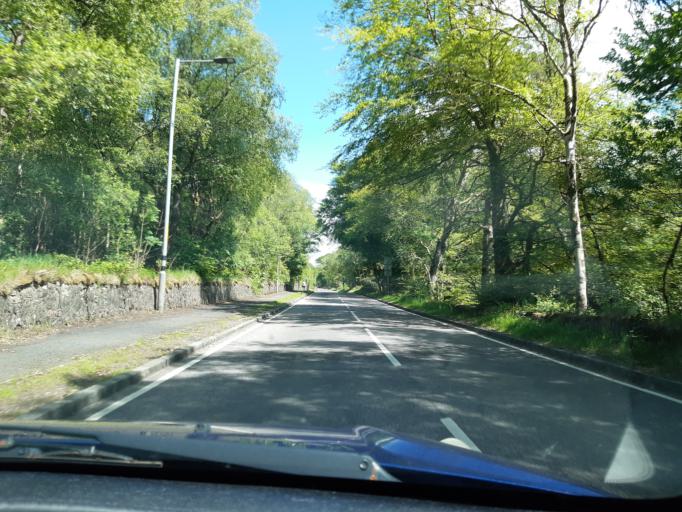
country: GB
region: Scotland
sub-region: Argyll and Bute
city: Garelochhead
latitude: 56.1983
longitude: -4.7415
